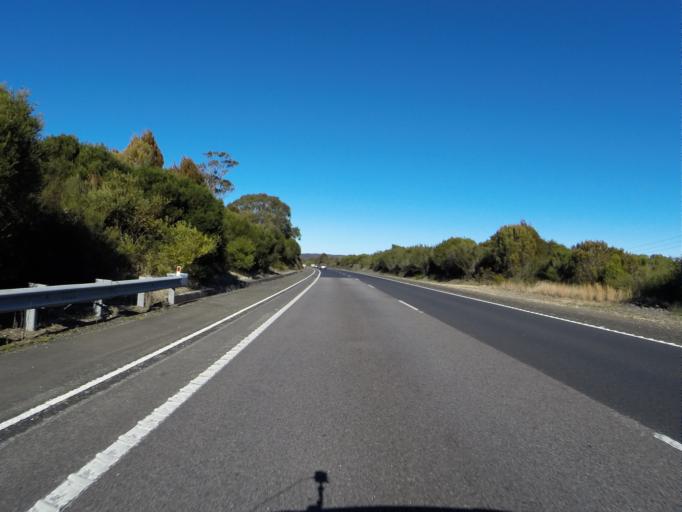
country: AU
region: New South Wales
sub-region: Wollongong
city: Bulli
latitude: -34.2633
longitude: 150.9286
